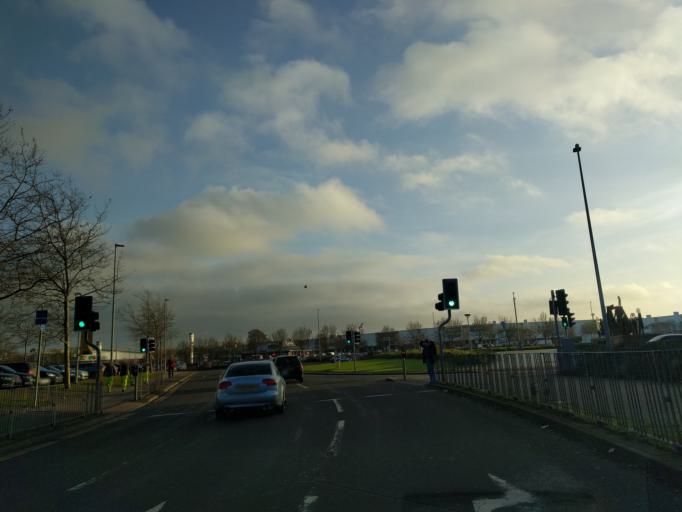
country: GB
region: England
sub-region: Lincolnshire
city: Lincoln
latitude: 53.2271
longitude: -0.5502
